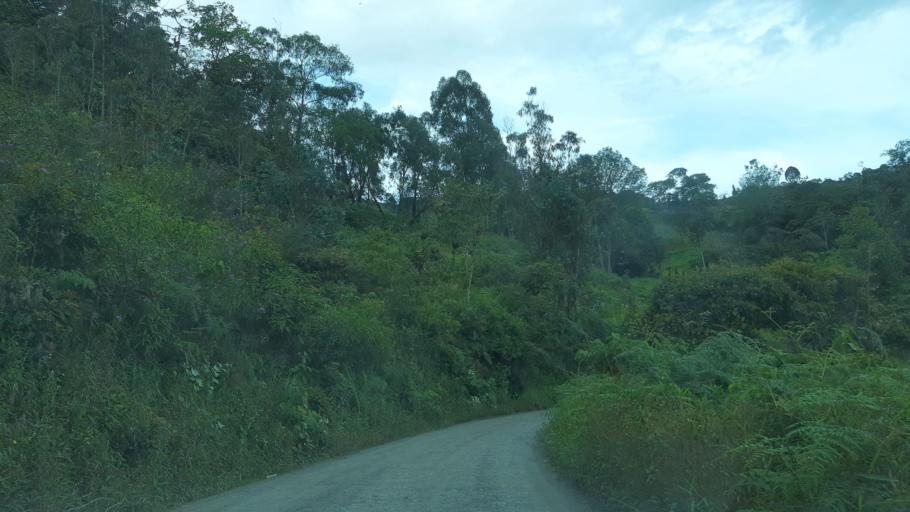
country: CO
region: Boyaca
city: Garagoa
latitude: 4.9864
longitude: -73.3237
